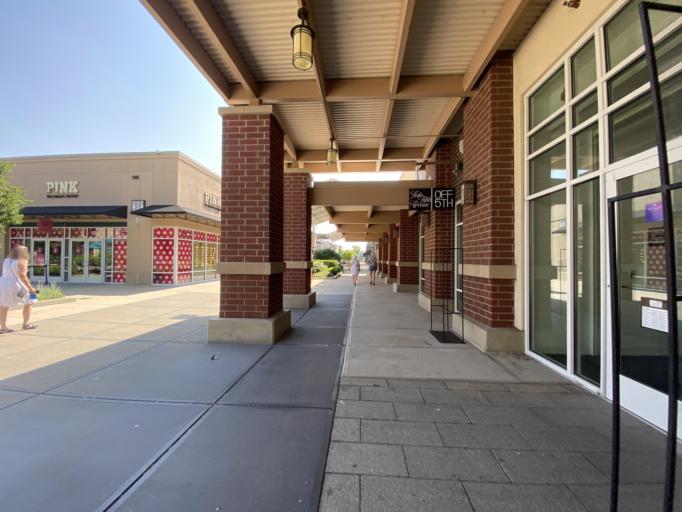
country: US
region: Illinois
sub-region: Kane County
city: North Aurora
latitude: 41.8006
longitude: -88.2701
